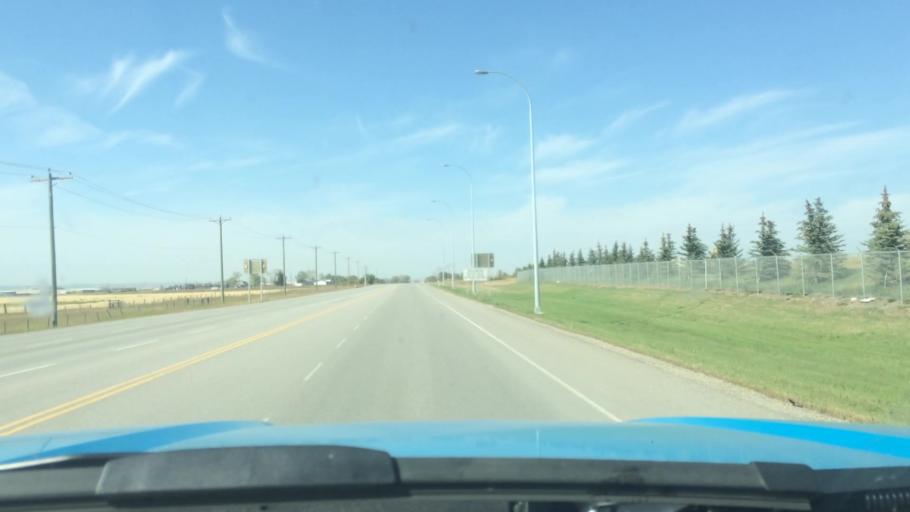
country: CA
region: Alberta
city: Airdrie
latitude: 51.2134
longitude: -113.9367
